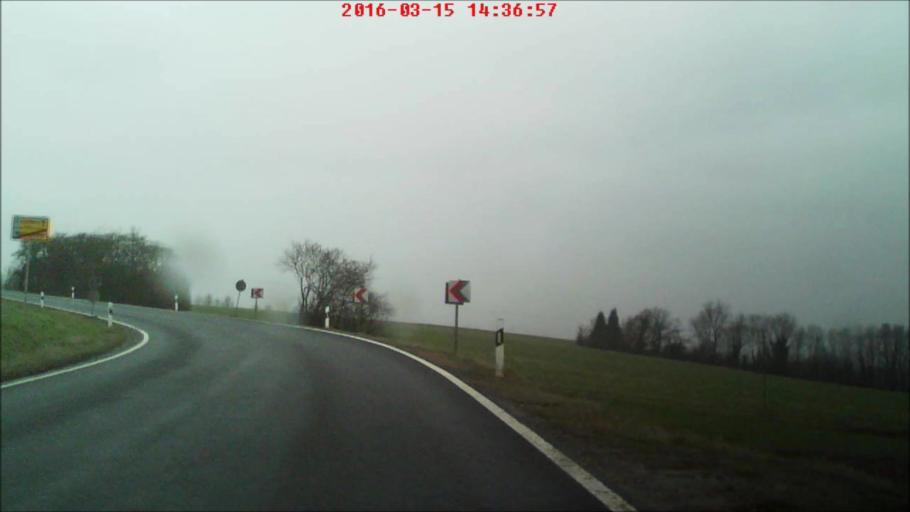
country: DE
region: Thuringia
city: Elxleben
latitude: 50.8870
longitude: 11.0618
